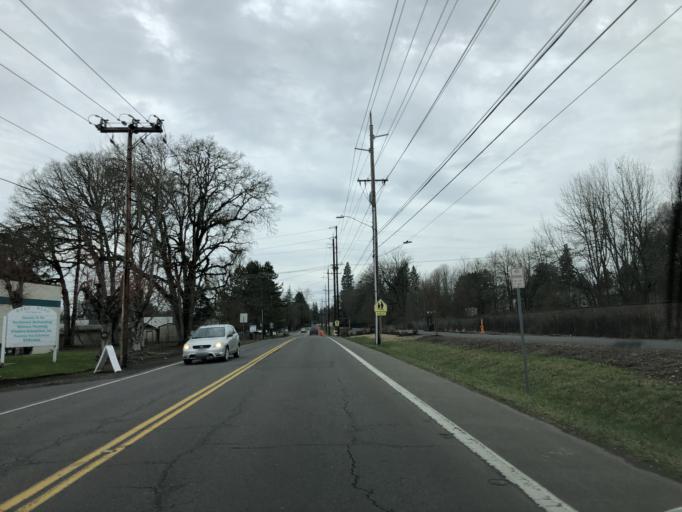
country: US
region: Oregon
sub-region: Washington County
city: Tigard
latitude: 45.4319
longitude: -122.7742
